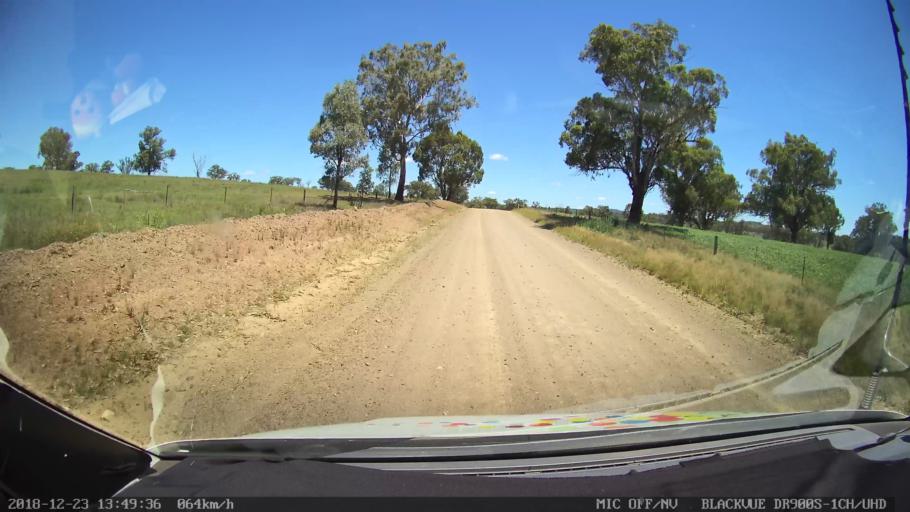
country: AU
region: New South Wales
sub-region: Tamworth Municipality
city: Manilla
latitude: -30.5229
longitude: 151.1081
